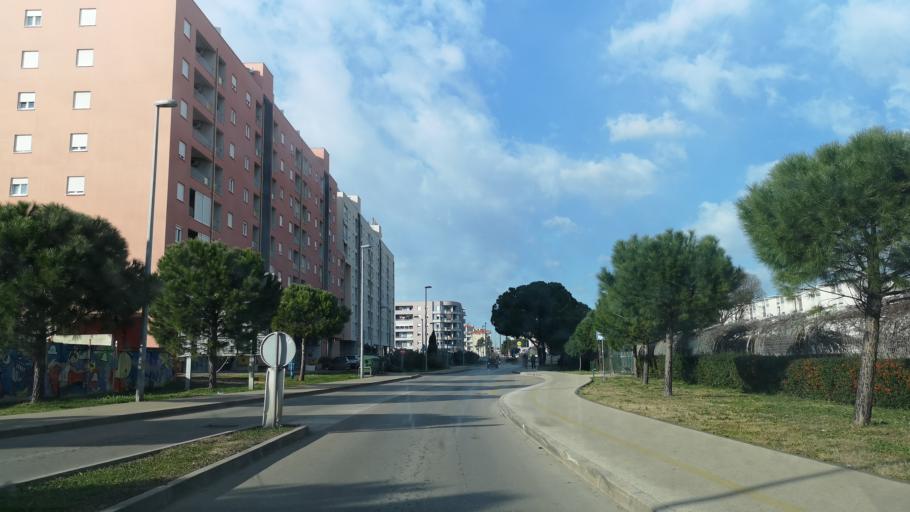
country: HR
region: Zadarska
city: Zadar
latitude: 44.1210
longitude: 15.2392
